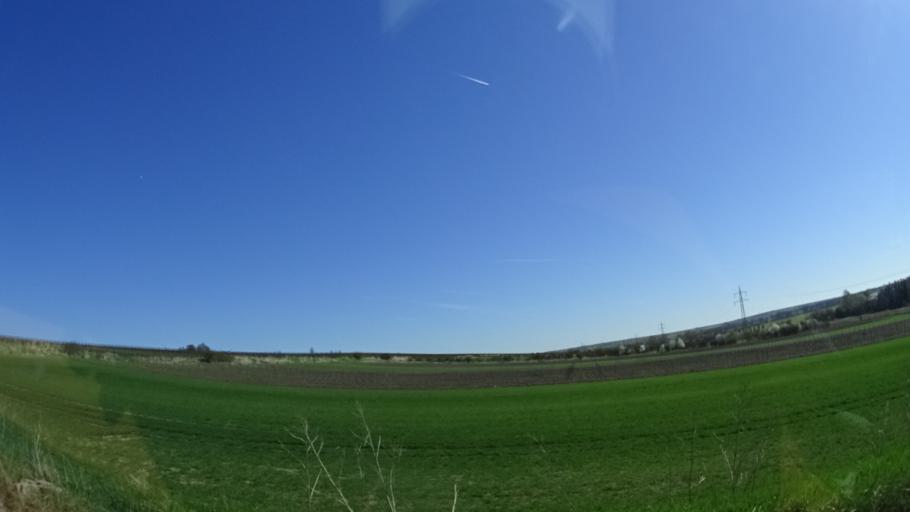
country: DE
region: Rheinland-Pfalz
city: Friesenheim
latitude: 49.8388
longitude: 8.2565
